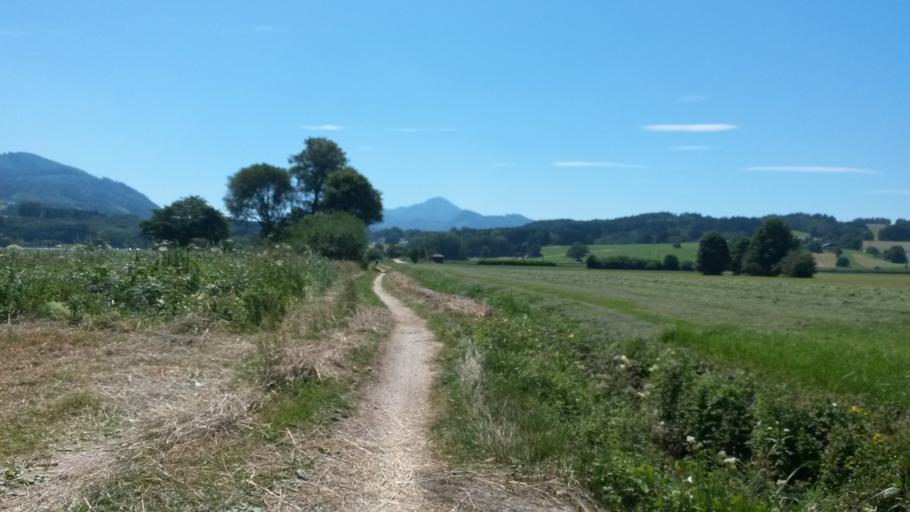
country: DE
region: Bavaria
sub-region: Upper Bavaria
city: Bernau am Chiemsee
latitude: 47.8246
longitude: 12.3715
